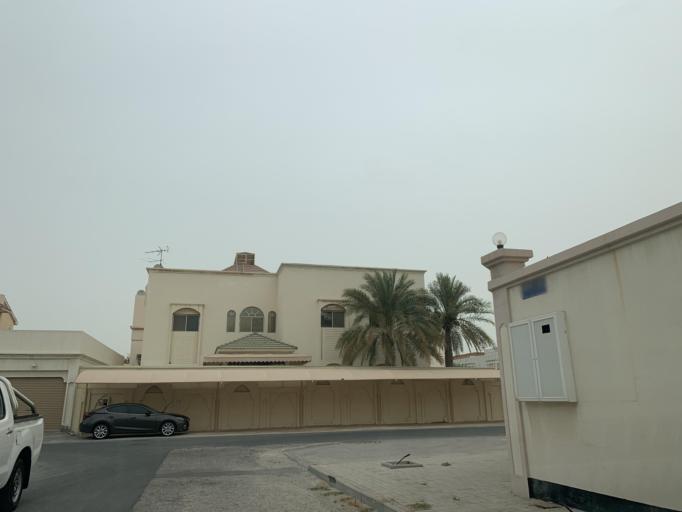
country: BH
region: Northern
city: Ar Rifa'
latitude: 26.1470
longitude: 50.5268
